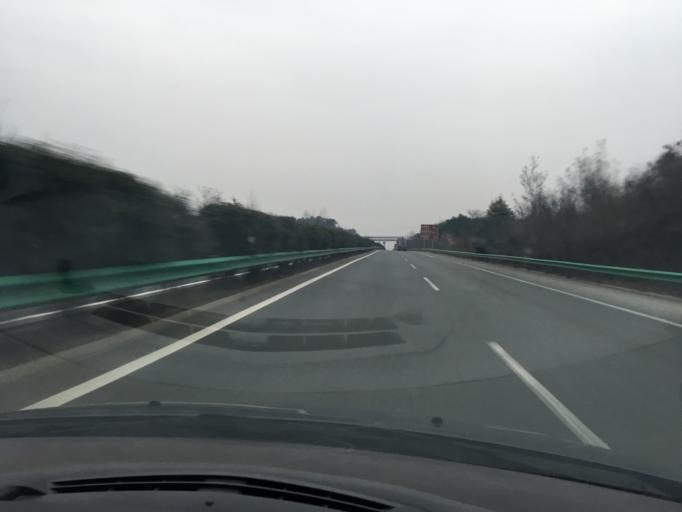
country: CN
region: Hubei
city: Yongjiahe
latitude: 31.0909
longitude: 114.7142
